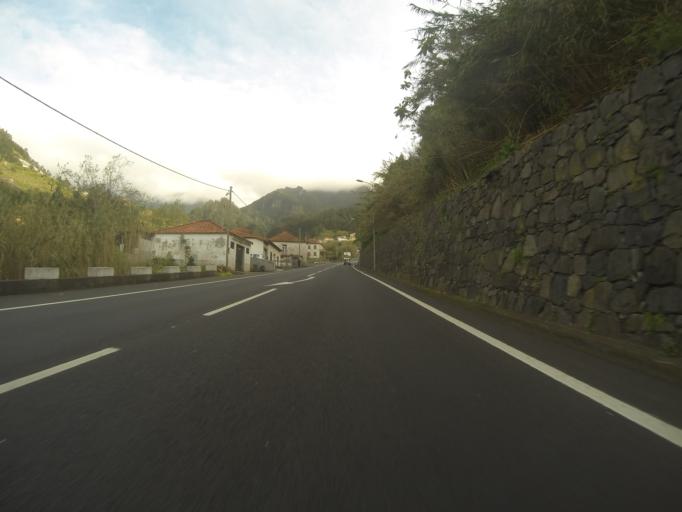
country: PT
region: Madeira
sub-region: Sao Vicente
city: Sao Vicente
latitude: 32.7770
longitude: -17.0330
